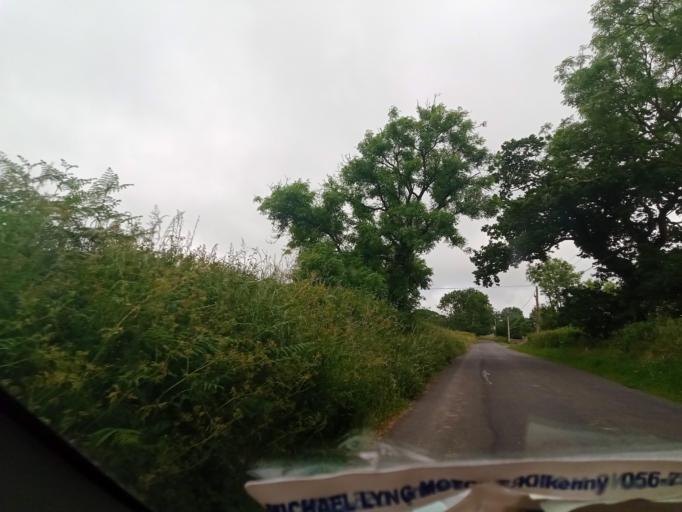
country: IE
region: Leinster
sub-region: Kilkenny
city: Ballyragget
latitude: 52.7498
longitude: -7.4304
